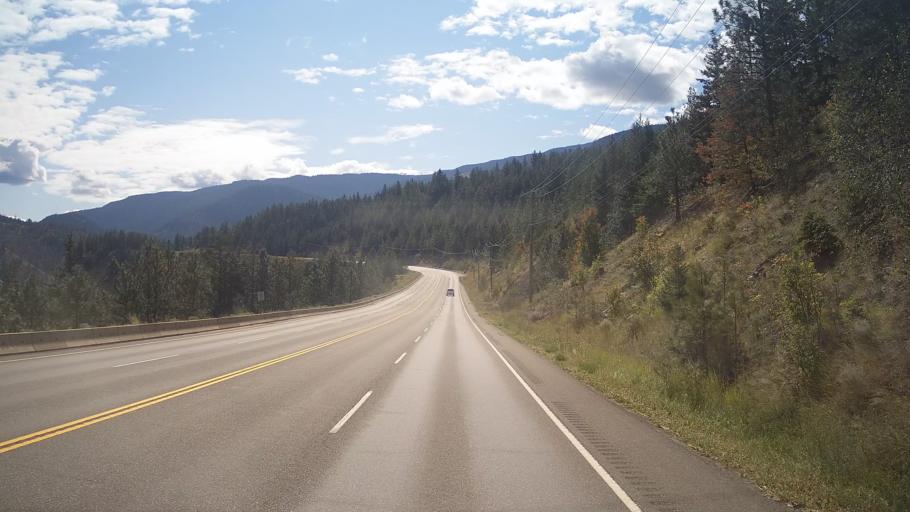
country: CA
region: British Columbia
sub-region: Thompson-Nicola Regional District
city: Ashcroft
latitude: 50.2563
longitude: -121.5229
